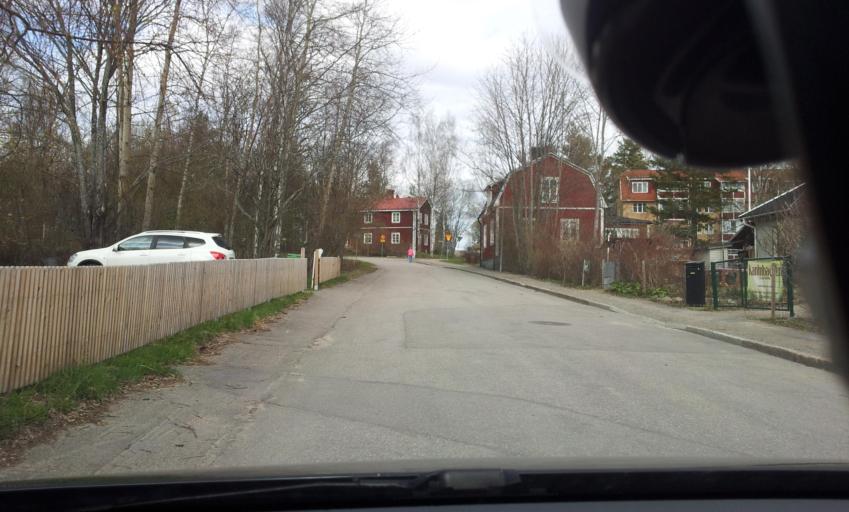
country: SE
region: Gaevleborg
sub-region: Ljusdals Kommun
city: Ljusdal
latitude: 61.8308
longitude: 16.0924
